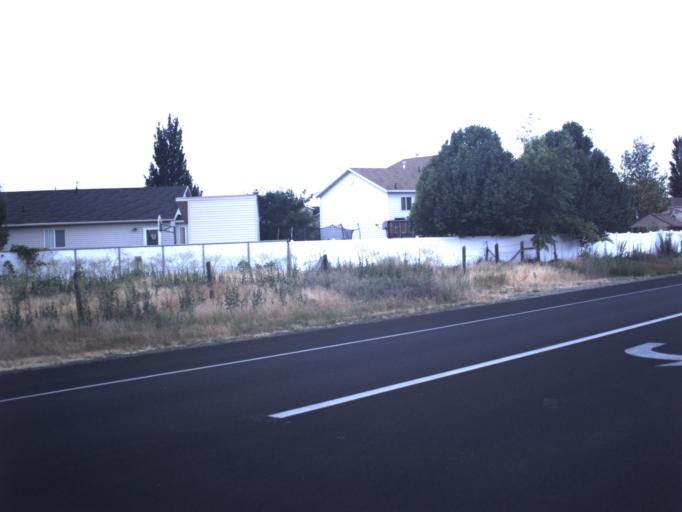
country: US
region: Utah
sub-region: Davis County
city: Clinton
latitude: 41.1627
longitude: -112.0687
